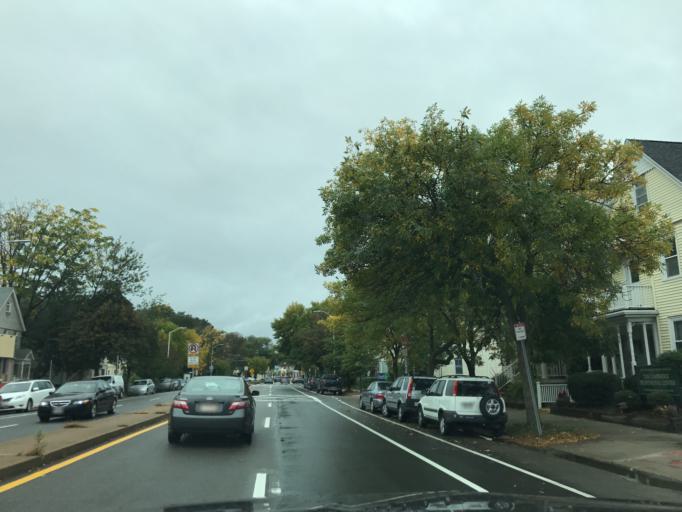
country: US
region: Massachusetts
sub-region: Middlesex County
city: Arlington
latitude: 42.4001
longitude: -71.1340
